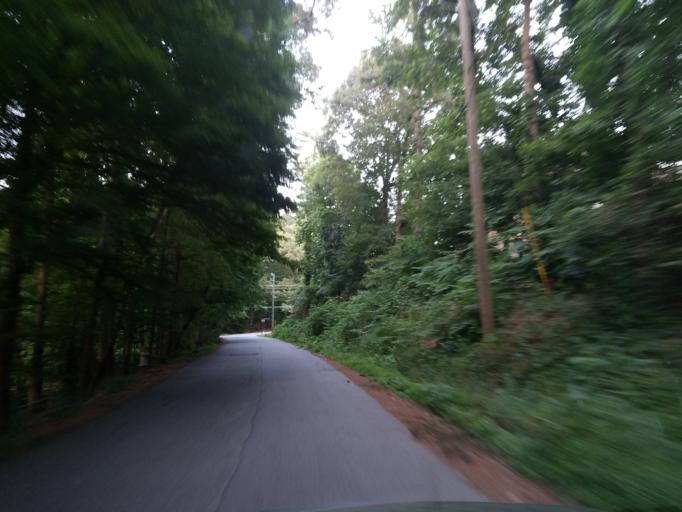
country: US
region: Georgia
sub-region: Cobb County
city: Vinings
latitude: 33.8685
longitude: -84.4639
